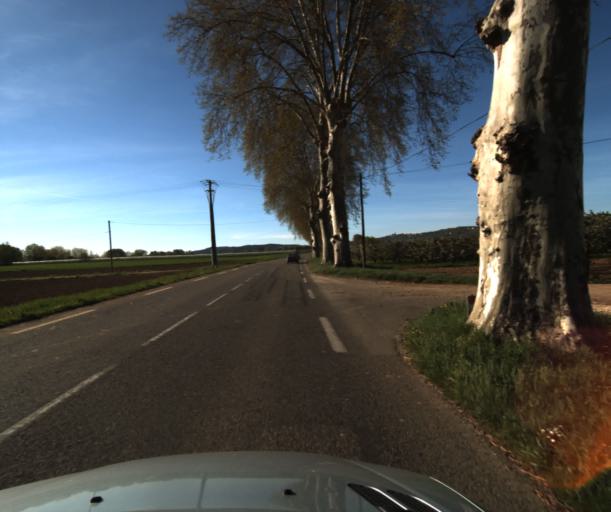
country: FR
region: Midi-Pyrenees
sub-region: Departement du Tarn-et-Garonne
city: Lafrancaise
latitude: 44.0937
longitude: 1.2629
